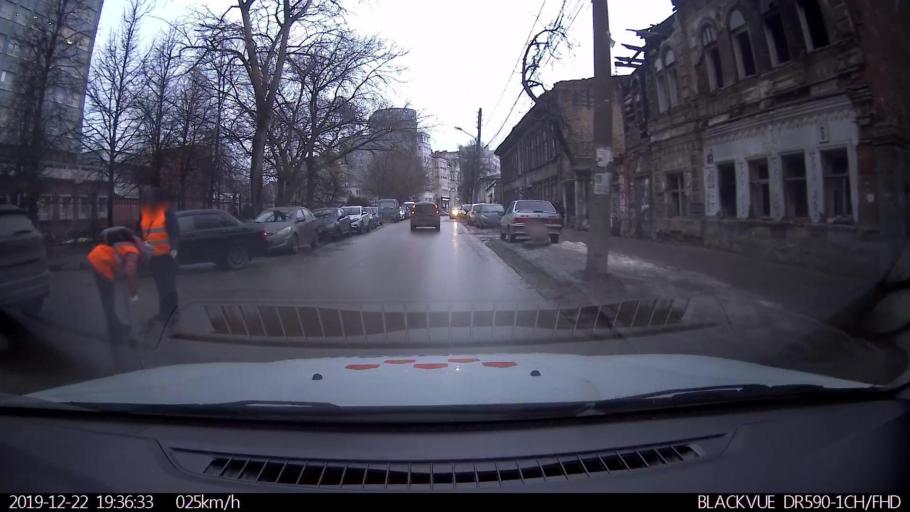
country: RU
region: Nizjnij Novgorod
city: Nizhniy Novgorod
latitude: 56.3183
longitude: 43.9858
